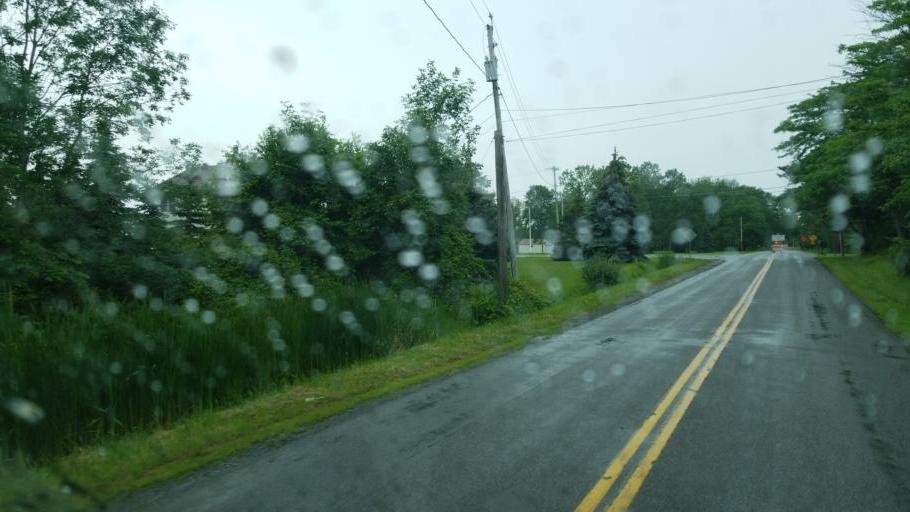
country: US
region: New York
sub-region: Niagara County
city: Ransomville
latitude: 43.2640
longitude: -78.8912
